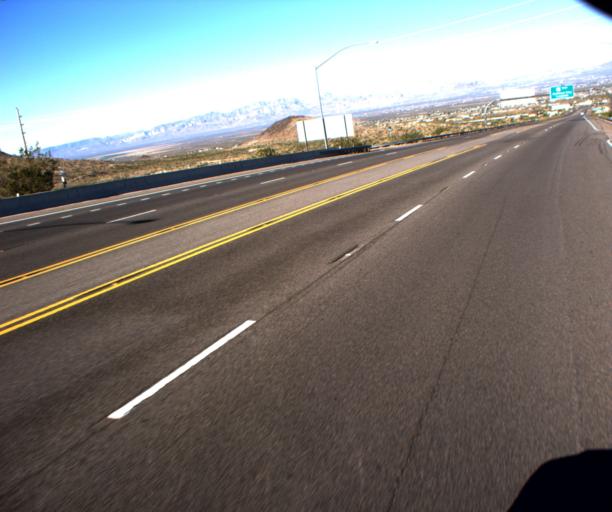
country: US
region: Arizona
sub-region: Mohave County
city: Kingman
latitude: 35.2197
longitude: -114.1309
